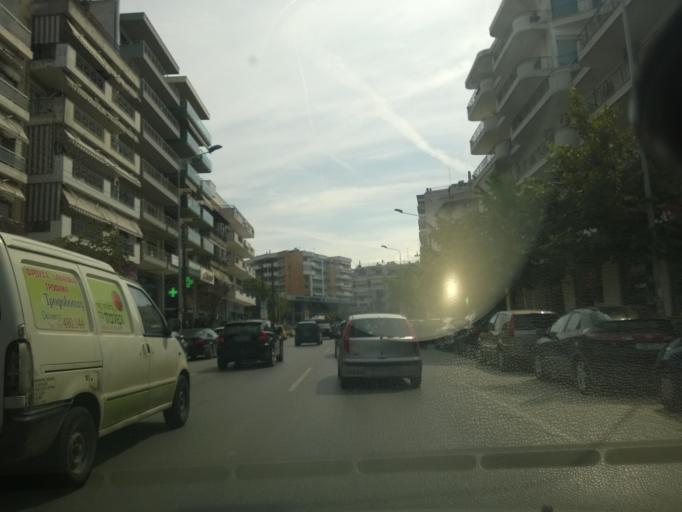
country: GR
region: Central Macedonia
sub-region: Nomos Thessalonikis
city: Kalamaria
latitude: 40.5847
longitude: 22.9577
